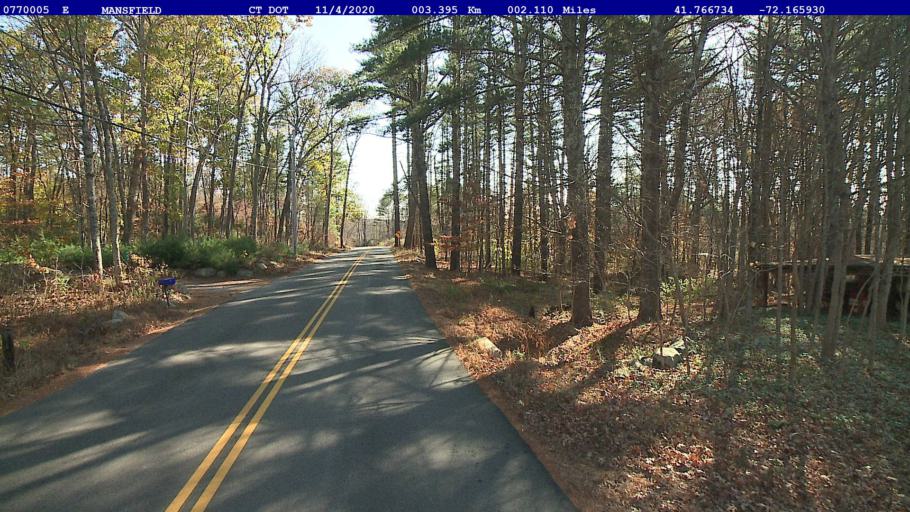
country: US
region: Connecticut
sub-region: Windham County
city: Windham
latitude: 41.7667
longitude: -72.1659
